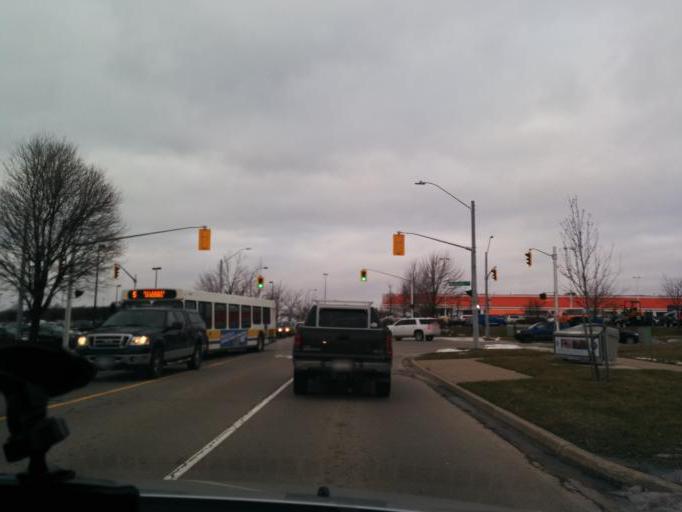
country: CA
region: Ontario
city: Ancaster
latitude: 43.2285
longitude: -79.9449
